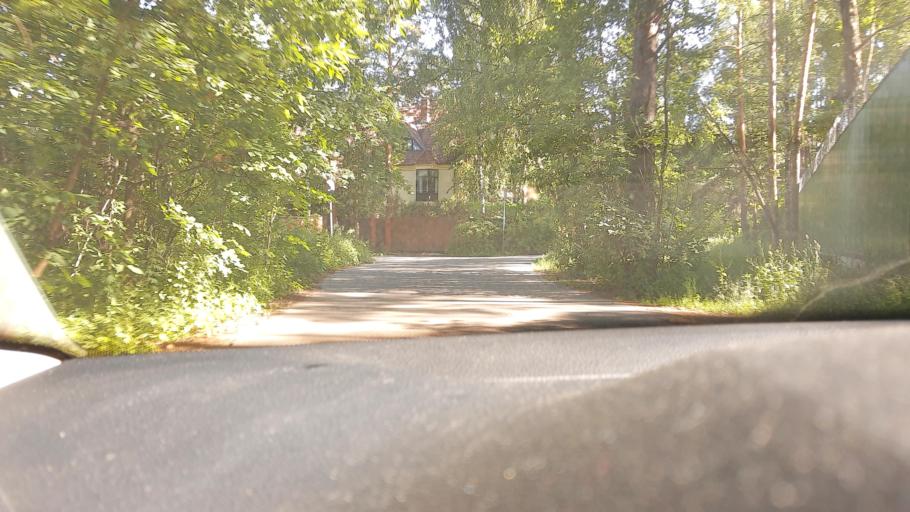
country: RU
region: Moscow
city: Rublevo
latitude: 55.7810
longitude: 37.3883
